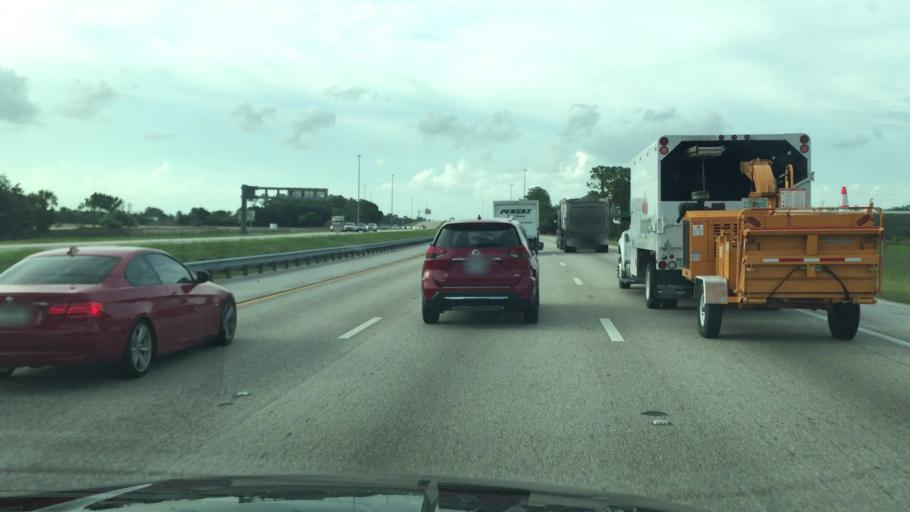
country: US
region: Florida
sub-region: Lee County
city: Tice
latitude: 26.6481
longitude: -81.7991
